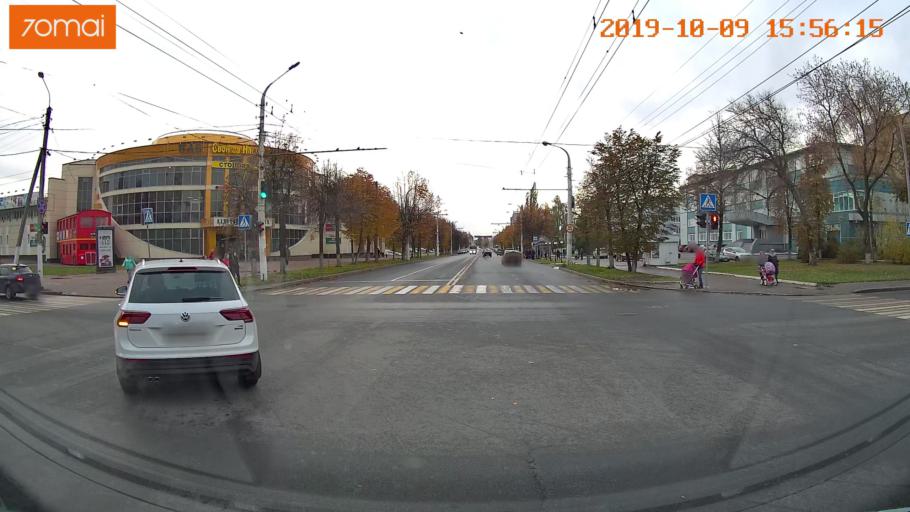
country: RU
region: Kostroma
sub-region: Kostromskoy Rayon
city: Kostroma
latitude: 57.7754
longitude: 40.9443
